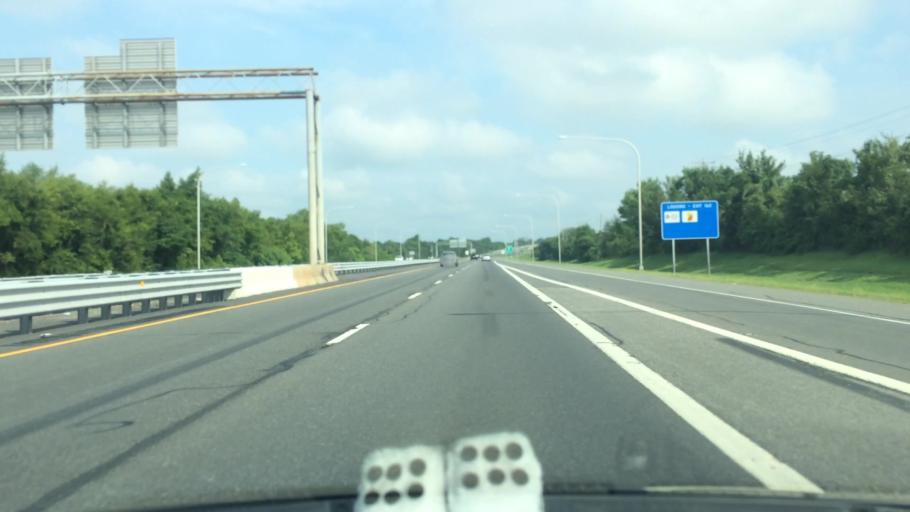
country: US
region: Delaware
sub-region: New Castle County
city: Bear
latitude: 39.6225
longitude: -75.6468
